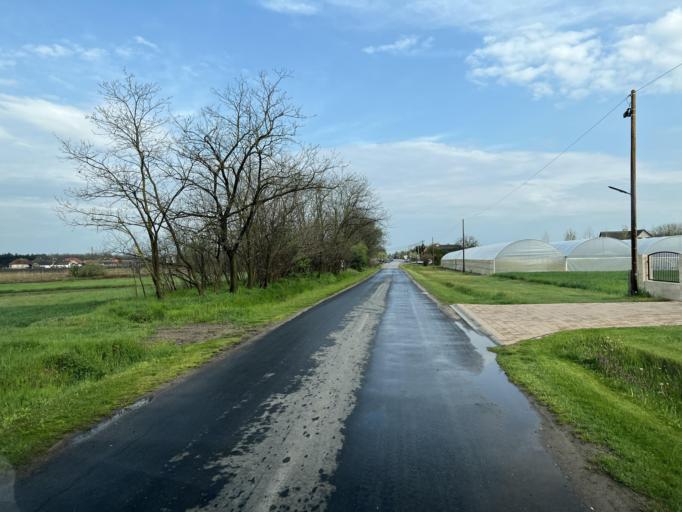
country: HU
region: Pest
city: Nyaregyhaza
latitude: 47.2205
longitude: 19.4603
